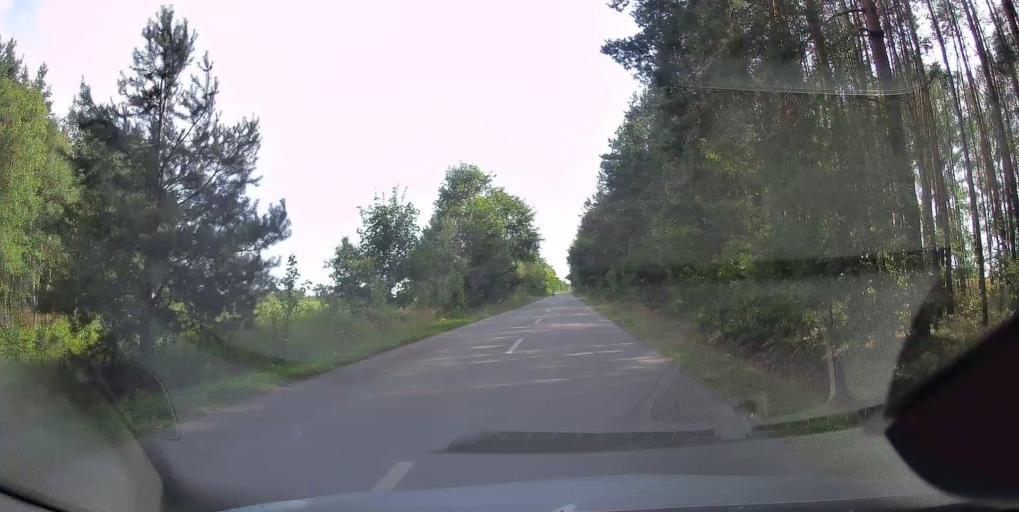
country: PL
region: Lodz Voivodeship
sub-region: Powiat opoczynski
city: Mniszkow
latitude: 51.3922
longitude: 20.0357
